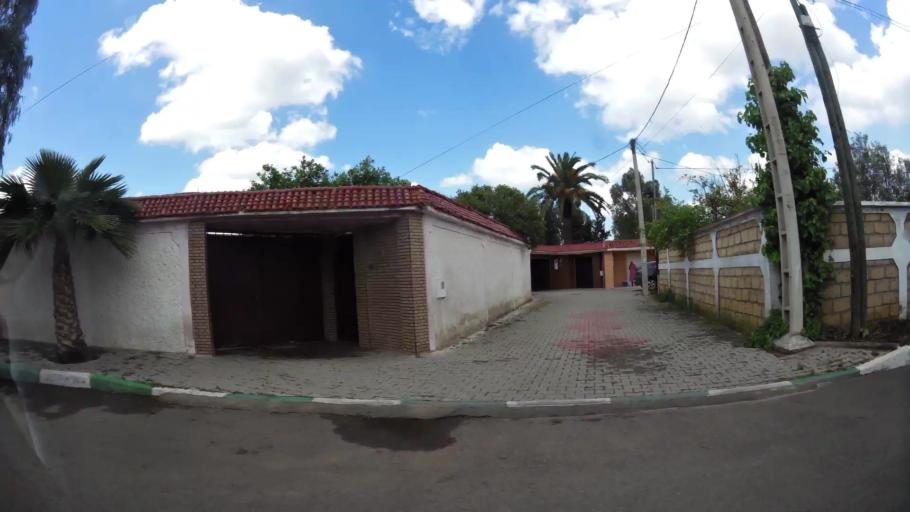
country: MA
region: Grand Casablanca
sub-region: Mediouna
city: Mediouna
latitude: 33.3869
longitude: -7.5408
